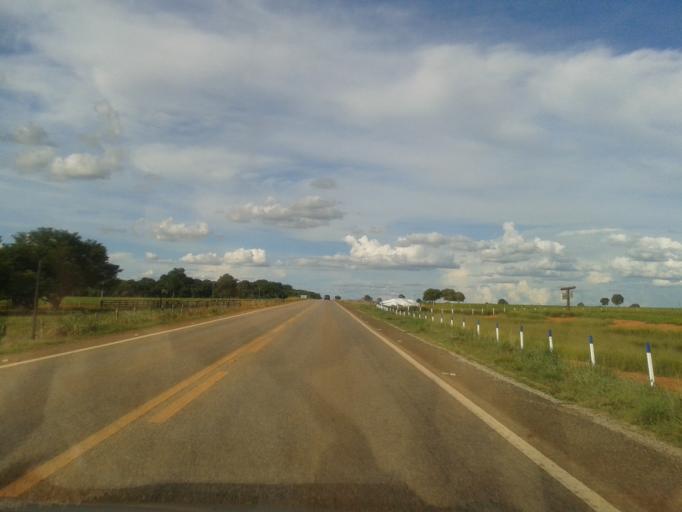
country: BR
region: Goias
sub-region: Mozarlandia
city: Mozarlandia
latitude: -14.3370
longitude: -50.4167
